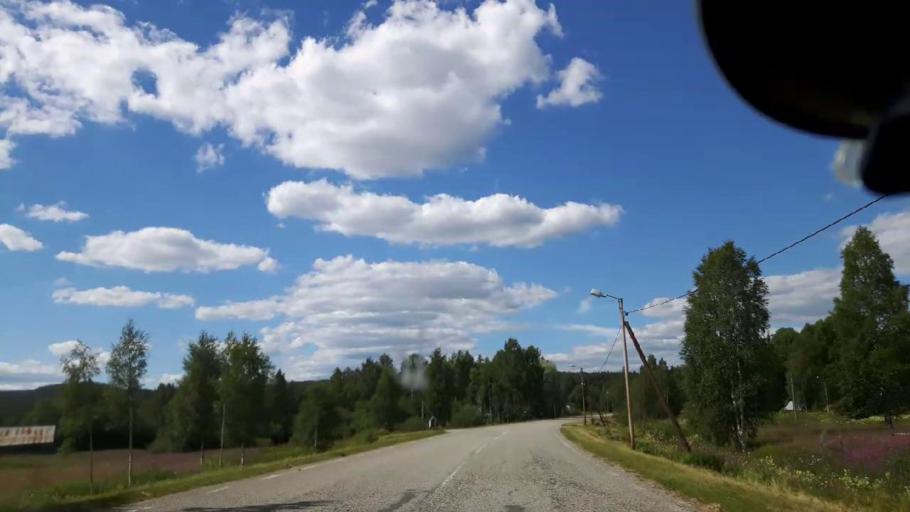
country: SE
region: Vaesternorrland
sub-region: Ange Kommun
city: Fransta
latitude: 62.7939
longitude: 16.2126
